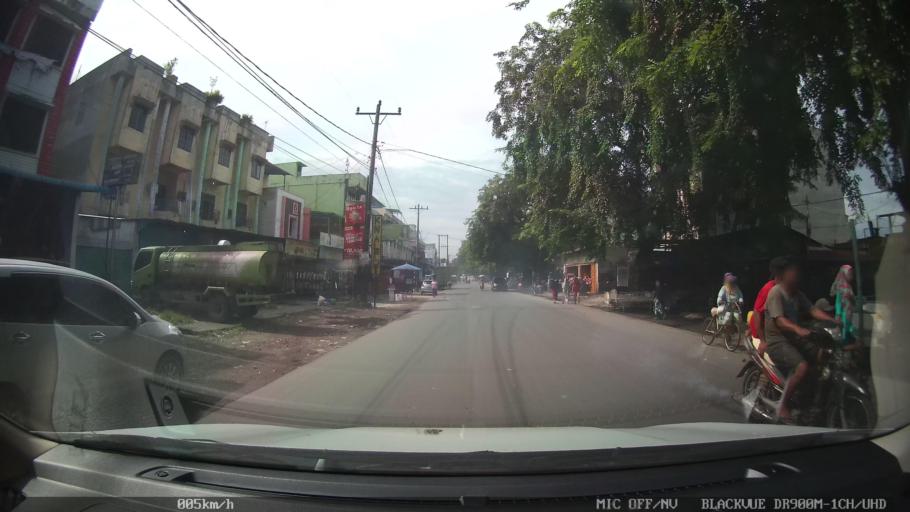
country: ID
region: North Sumatra
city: Sunggal
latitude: 3.6032
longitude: 98.6082
